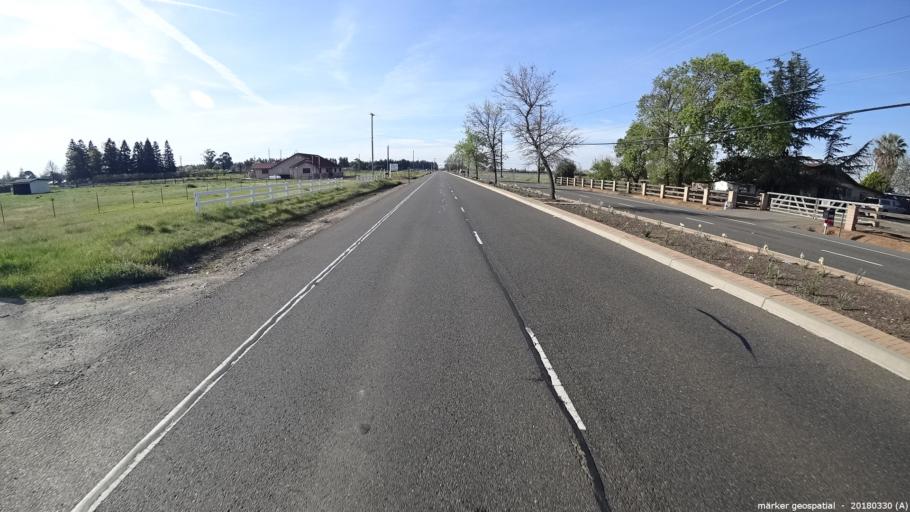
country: US
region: California
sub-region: Sacramento County
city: Rosemont
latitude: 38.5151
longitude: -121.3349
